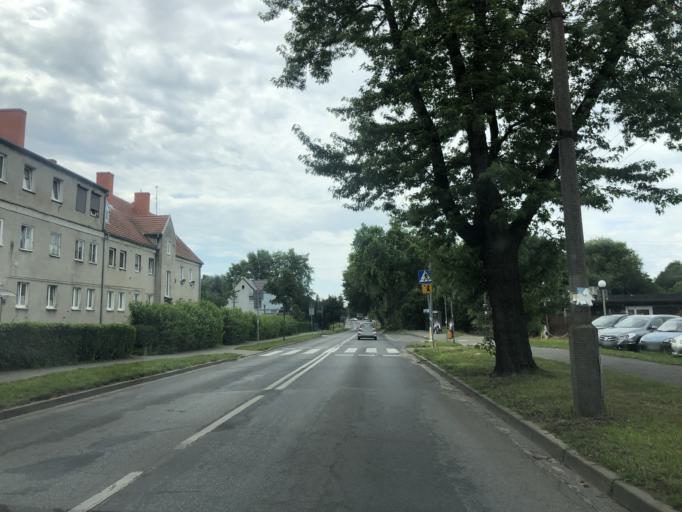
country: PL
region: Greater Poland Voivodeship
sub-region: Powiat poznanski
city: Lubon
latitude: 52.3660
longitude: 16.8952
